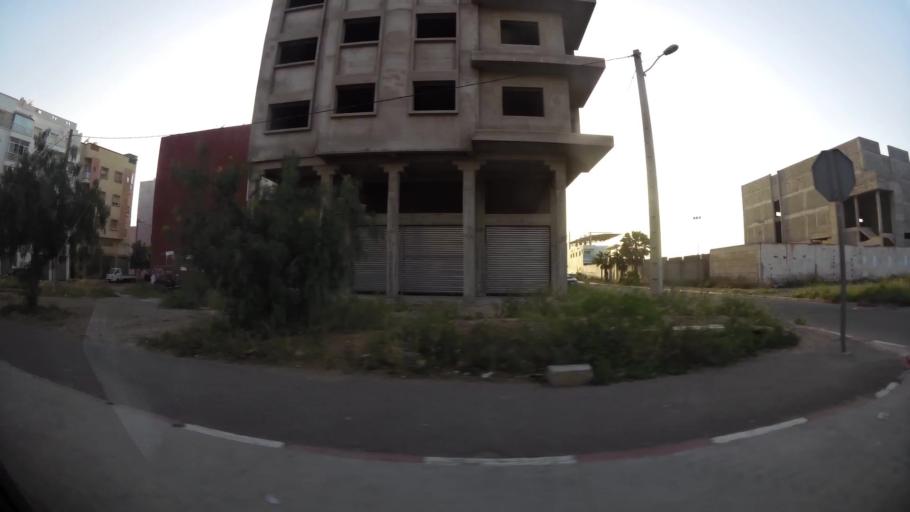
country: MA
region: Oued ed Dahab-Lagouira
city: Dakhla
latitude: 30.3951
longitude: -9.5653
